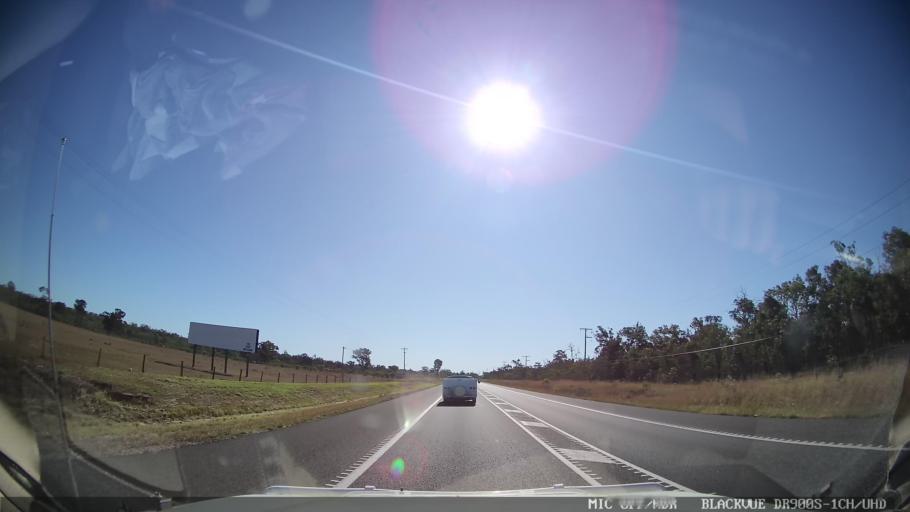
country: AU
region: Queensland
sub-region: Bundaberg
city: Childers
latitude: -25.2783
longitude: 152.3853
